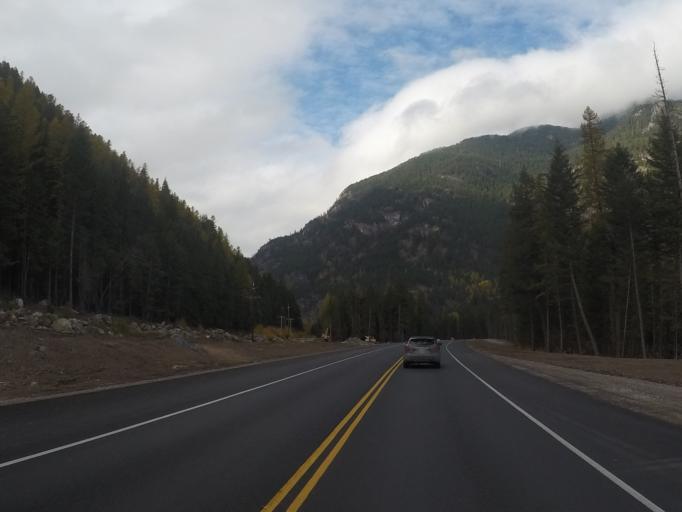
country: US
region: Montana
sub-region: Flathead County
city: Columbia Falls
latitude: 48.3861
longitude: -114.0867
